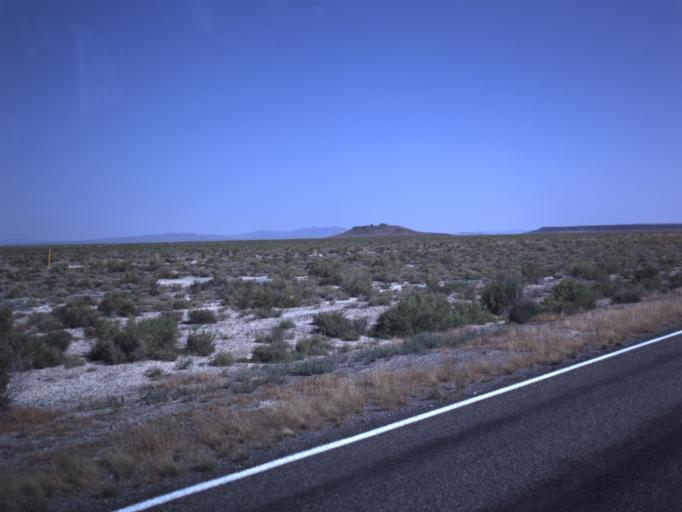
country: US
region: Utah
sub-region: Millard County
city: Delta
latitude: 39.0829
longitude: -112.7545
